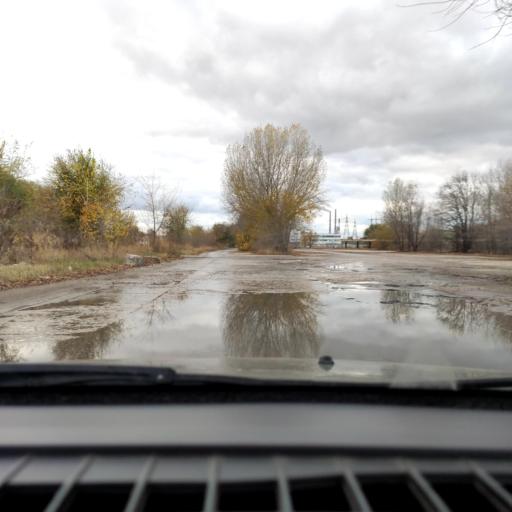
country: RU
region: Samara
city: Tol'yatti
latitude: 53.5644
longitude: 49.2957
